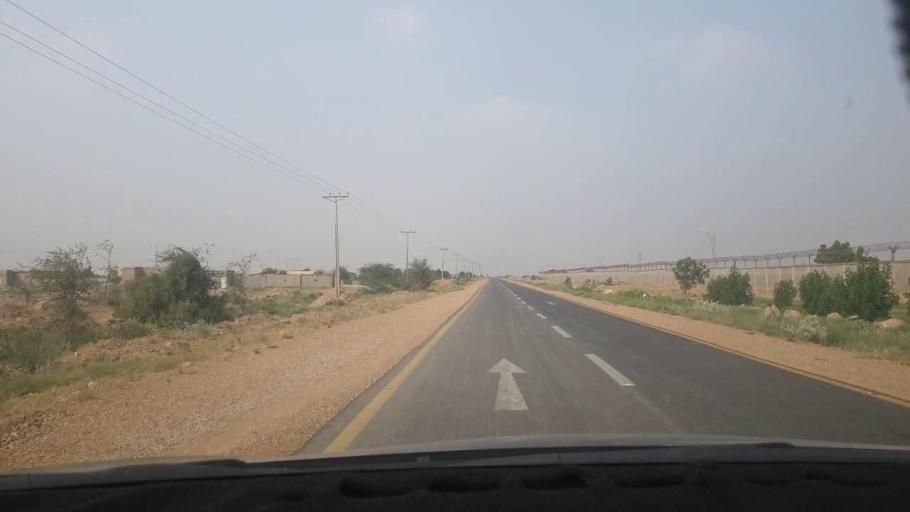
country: PK
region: Sindh
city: Jamshoro
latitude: 25.5614
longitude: 68.3182
